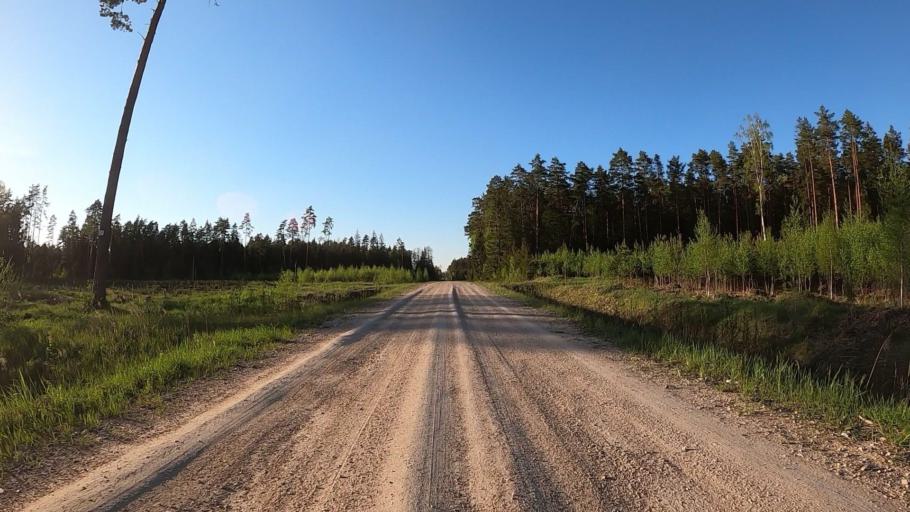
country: LV
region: Kekava
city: Kekava
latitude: 56.7617
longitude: 24.2227
